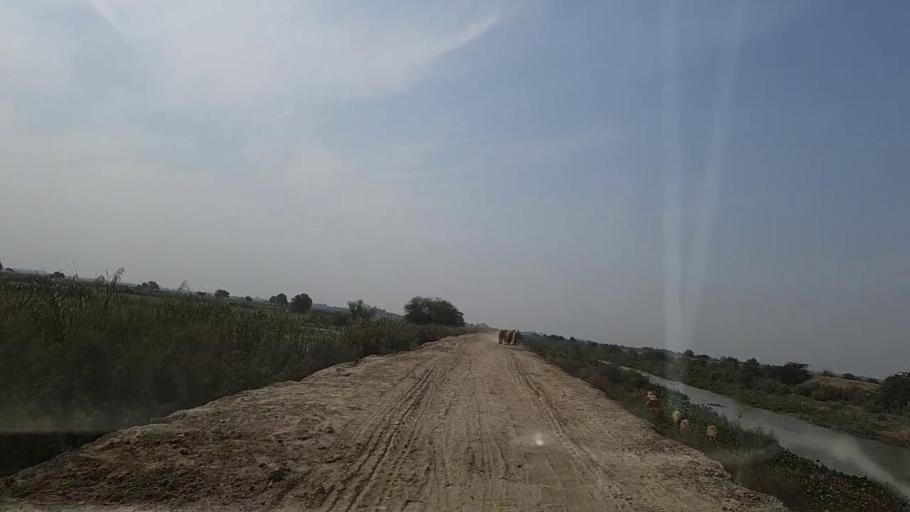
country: PK
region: Sindh
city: Mirpur Batoro
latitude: 24.6611
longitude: 68.2502
